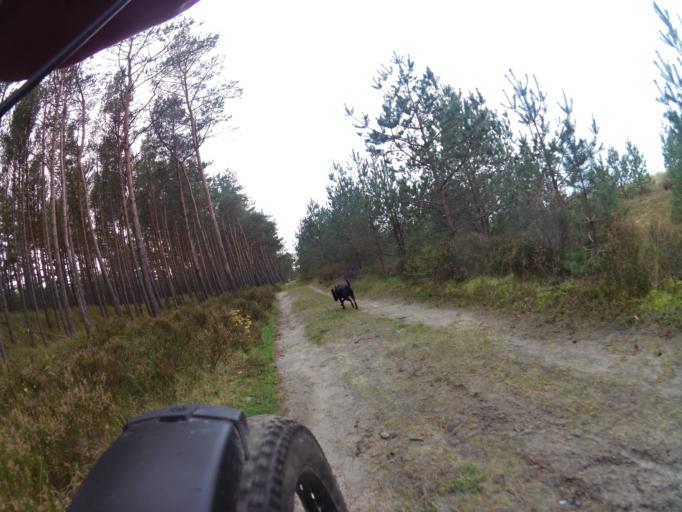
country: PL
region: Pomeranian Voivodeship
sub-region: Powiat wejherowski
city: Choczewo
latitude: 54.8075
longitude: 17.8095
